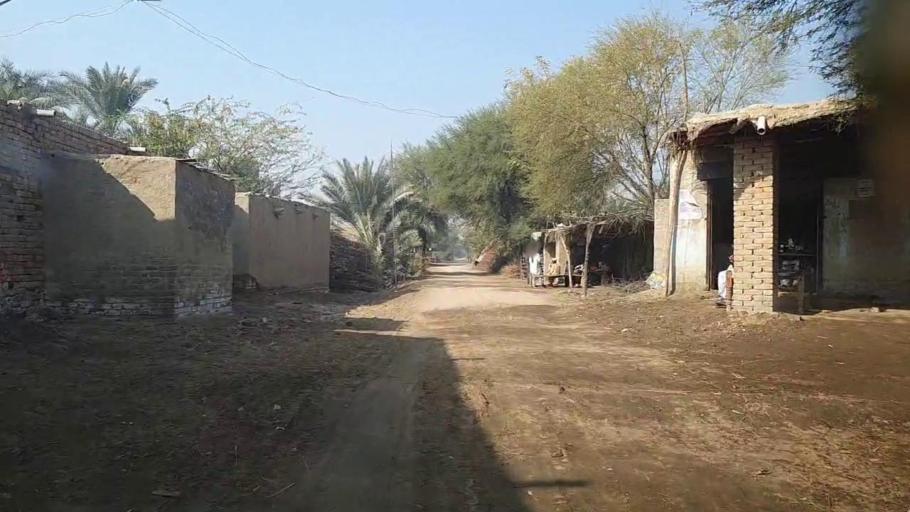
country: PK
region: Sindh
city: Karaundi
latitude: 26.8459
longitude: 68.3811
